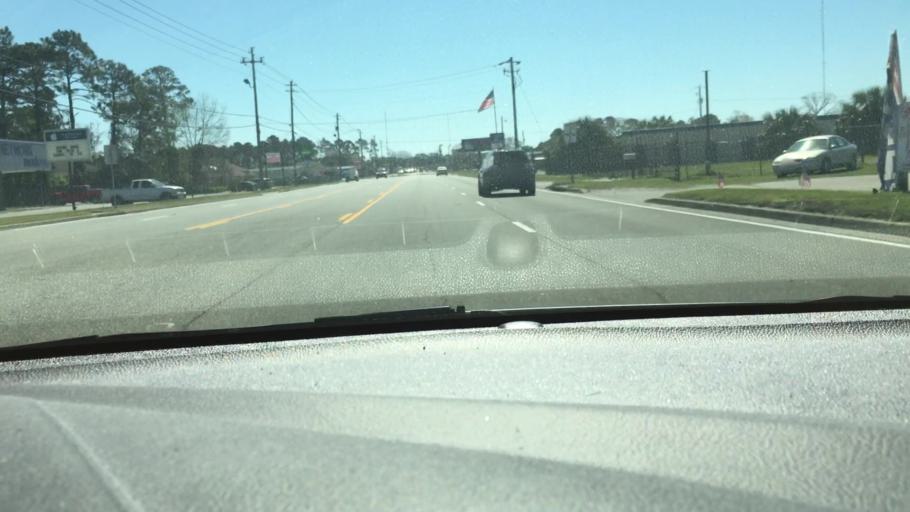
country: US
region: Georgia
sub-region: Glynn County
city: Dock Junction
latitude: 31.2014
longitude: -81.4942
